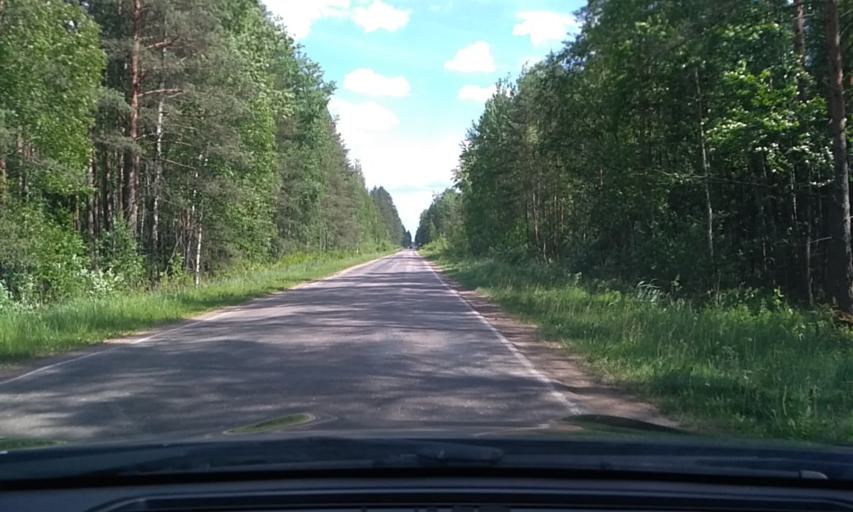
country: RU
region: Leningrad
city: Imeni Sverdlova
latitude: 59.8236
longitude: 30.7297
